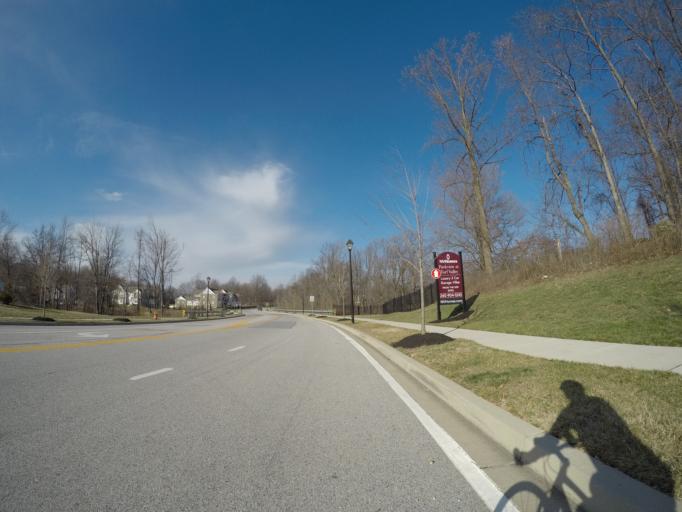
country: US
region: Maryland
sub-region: Howard County
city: Columbia
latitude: 39.3012
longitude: -76.8896
